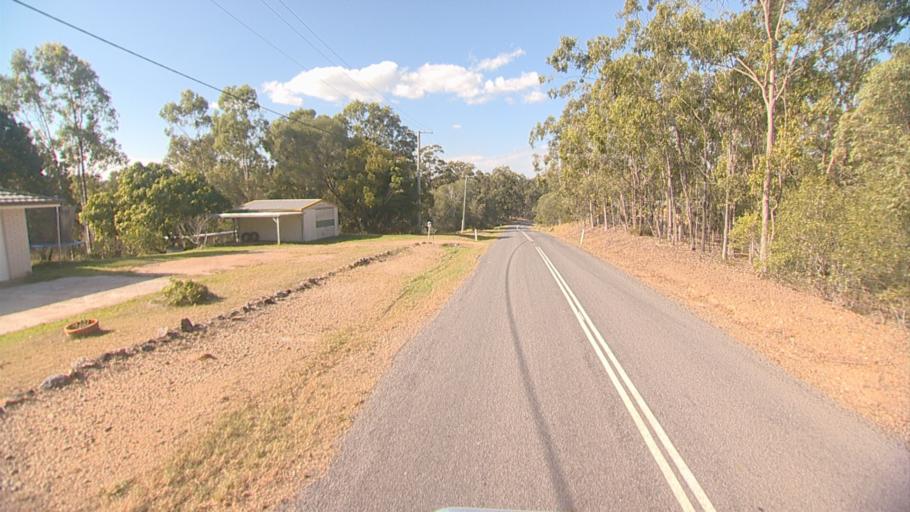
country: AU
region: Queensland
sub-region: Logan
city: Windaroo
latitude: -27.7389
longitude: 153.1617
